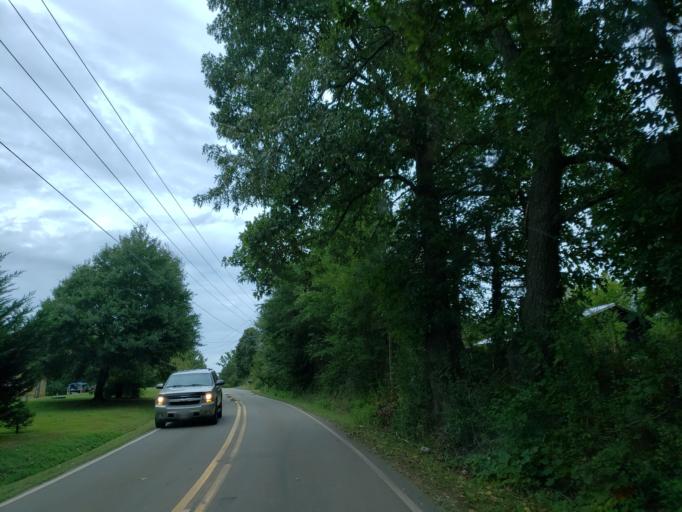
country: US
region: Georgia
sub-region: Pickens County
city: Jasper
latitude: 34.4254
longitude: -84.5519
